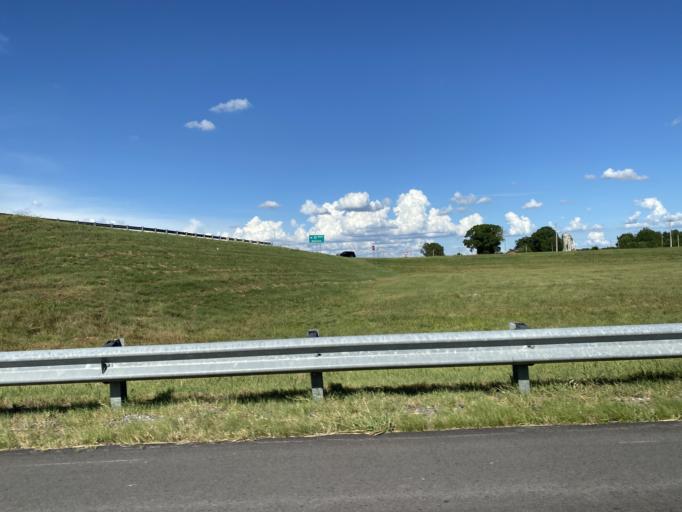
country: US
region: Alabama
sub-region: Limestone County
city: Athens
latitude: 34.7303
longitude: -86.9360
